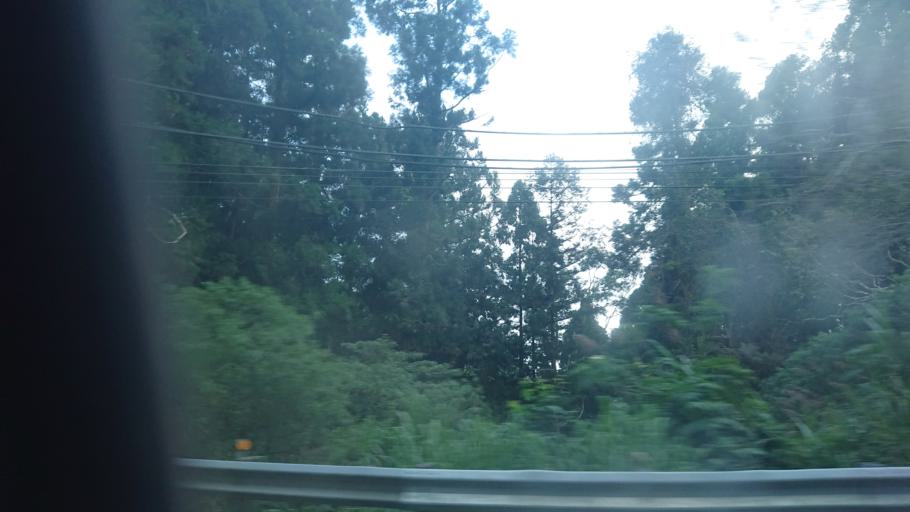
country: TW
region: Taiwan
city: Lugu
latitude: 23.4886
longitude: 120.7480
